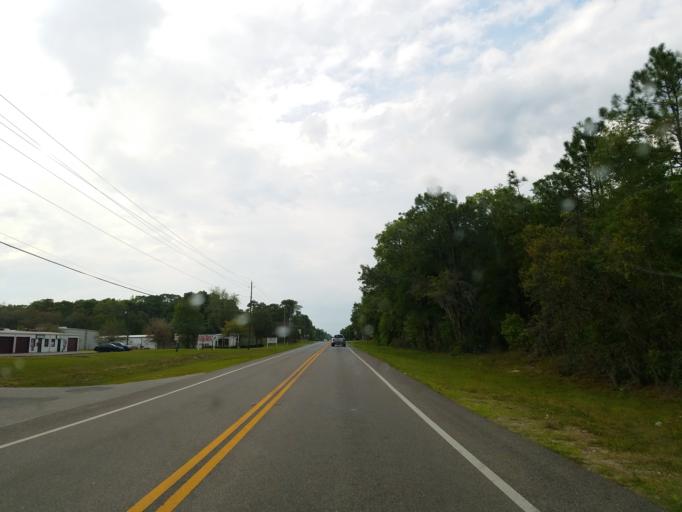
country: US
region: Florida
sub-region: Citrus County
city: Floral City
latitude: 28.7866
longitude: -82.3001
